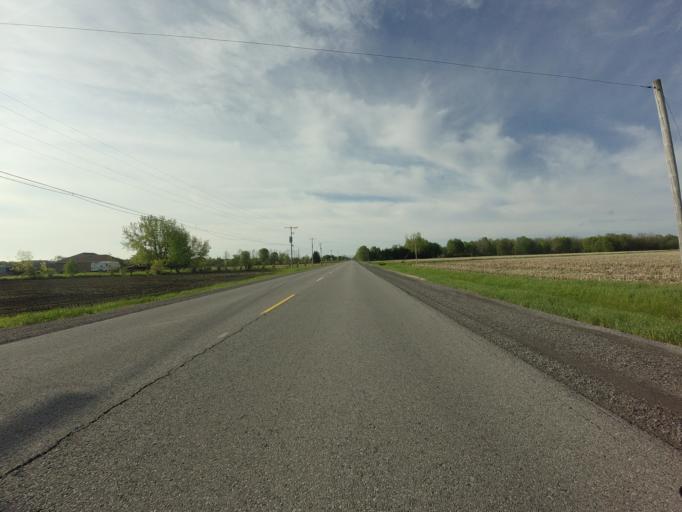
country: CA
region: Ontario
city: Ottawa
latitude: 45.2876
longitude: -75.4469
